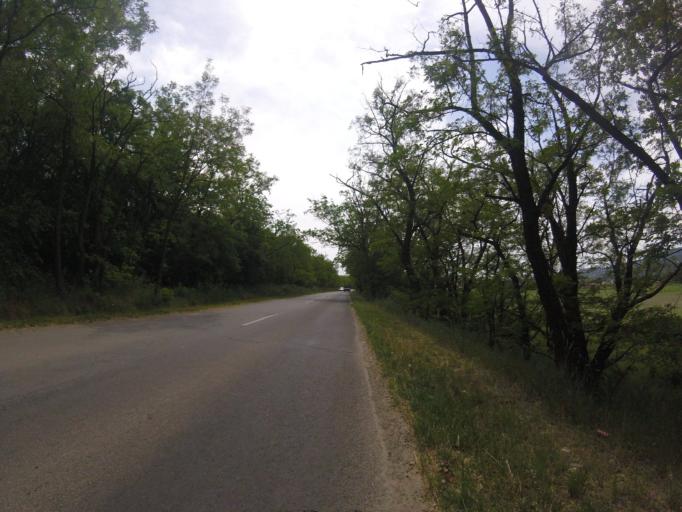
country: HU
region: Pest
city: Leanyfalu
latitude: 47.7226
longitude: 19.1046
